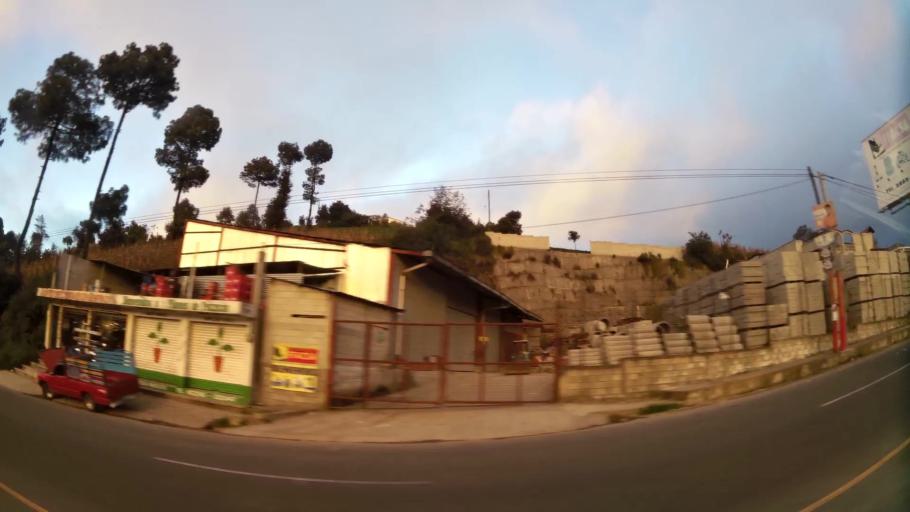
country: GT
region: Solola
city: Concepcion
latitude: 14.8510
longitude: -91.1465
